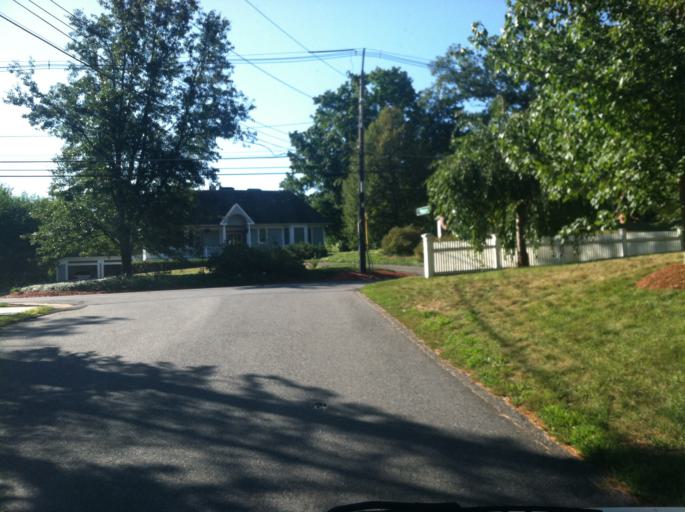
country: US
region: Massachusetts
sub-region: Middlesex County
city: Concord
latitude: 42.4702
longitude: -71.3268
